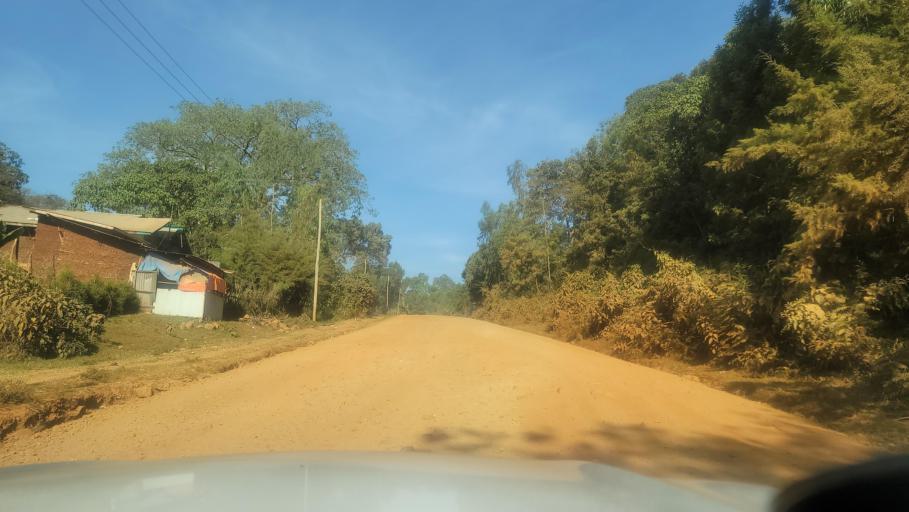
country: ET
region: Oromiya
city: Agaro
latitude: 7.8388
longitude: 36.5521
